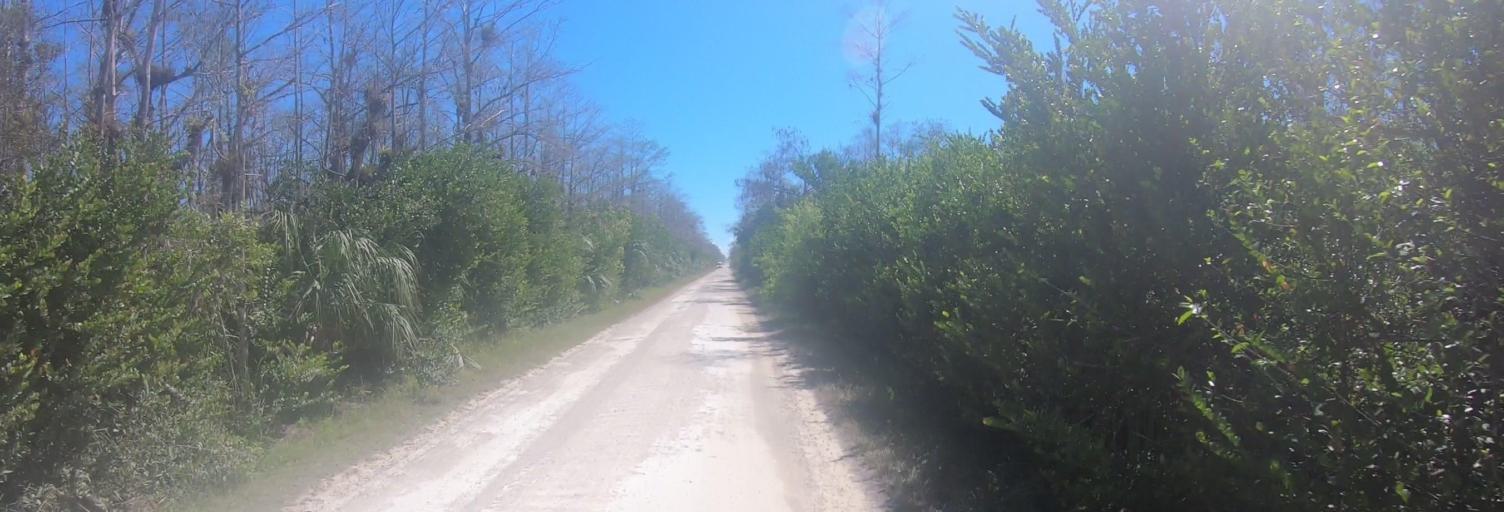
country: US
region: Florida
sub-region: Miami-Dade County
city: The Hammocks
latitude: 25.7588
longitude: -80.9914
